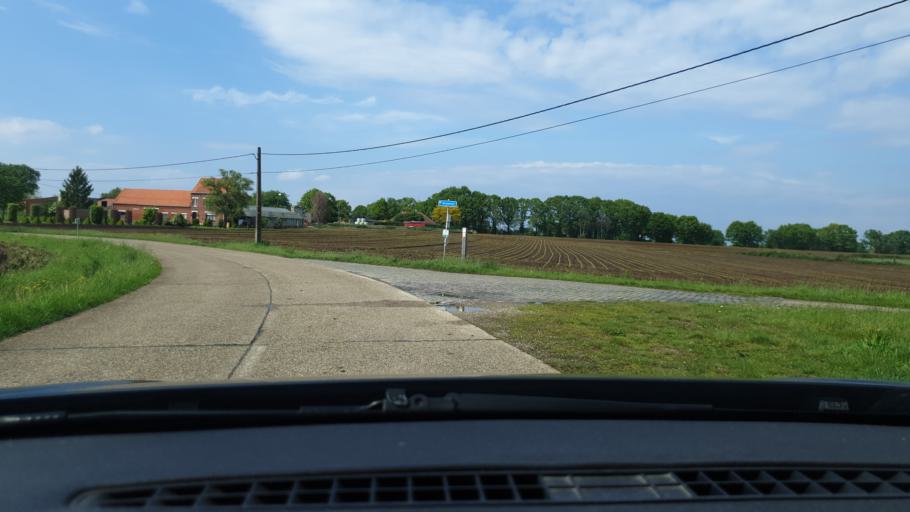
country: BE
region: Flanders
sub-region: Provincie Antwerpen
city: Meerhout
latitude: 51.1237
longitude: 5.1029
